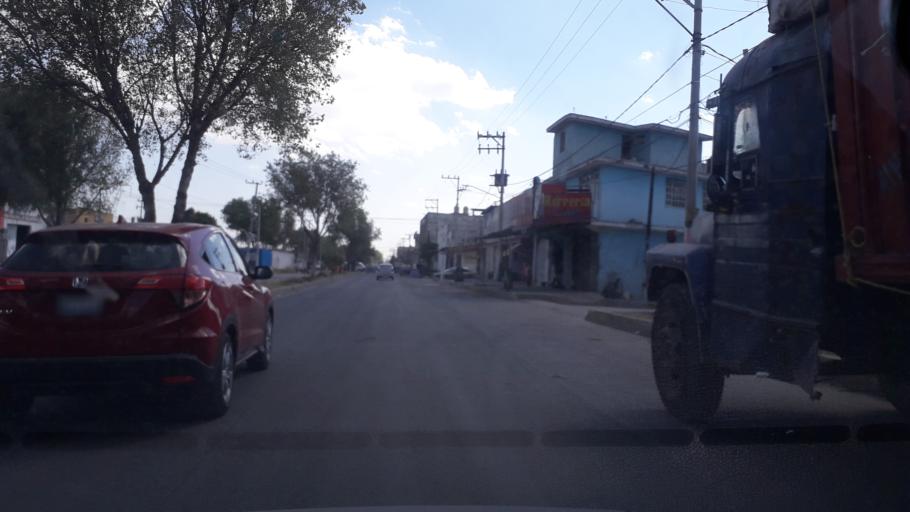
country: MX
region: Mexico
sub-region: Jaltenco
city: Alborada Jaltenco
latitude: 19.6469
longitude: -99.0623
